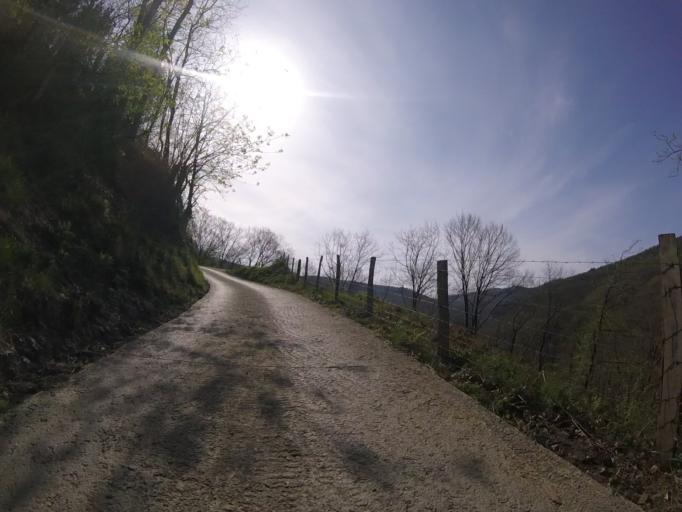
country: ES
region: Basque Country
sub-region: Provincia de Guipuzcoa
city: Errenteria
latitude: 43.2766
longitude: -1.8411
